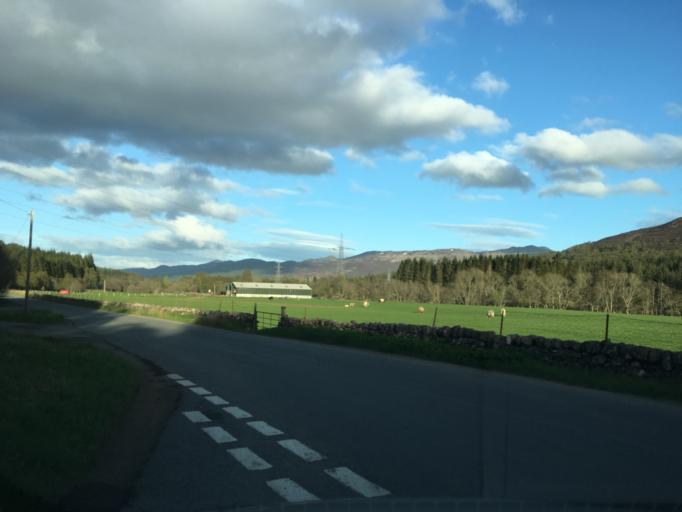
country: GB
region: Scotland
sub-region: Perth and Kinross
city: Aberfeldy
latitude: 56.7108
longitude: -4.0390
